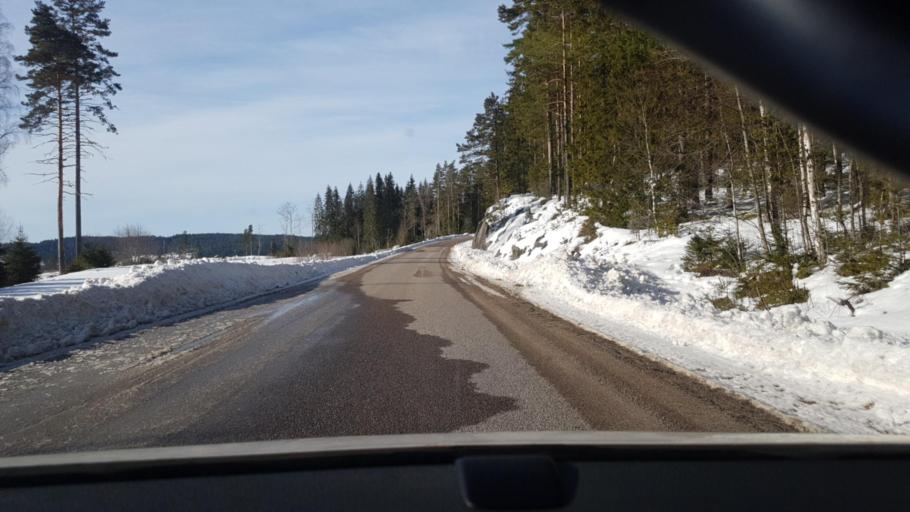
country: NO
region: Hedmark
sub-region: Eidskog
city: Skotterud
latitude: 59.8040
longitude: 12.0422
